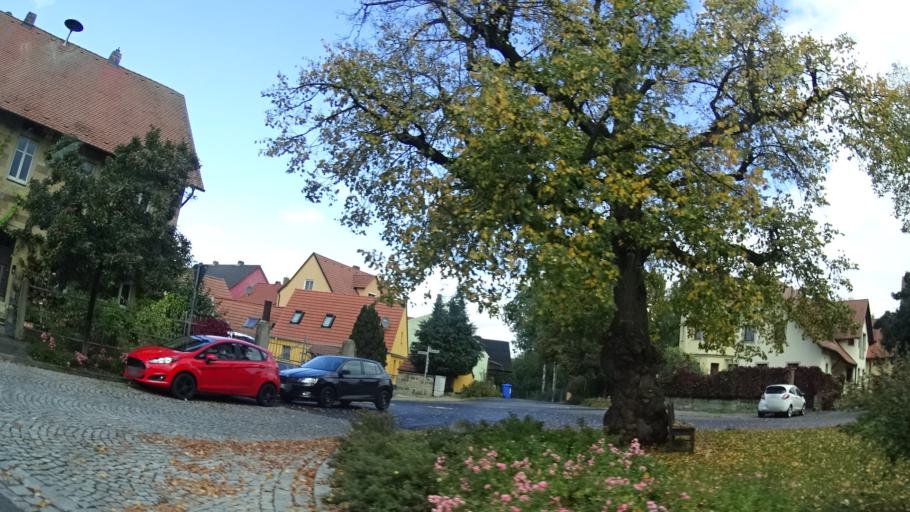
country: DE
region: Bavaria
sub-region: Regierungsbezirk Unterfranken
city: Frankenwinheim
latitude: 49.8639
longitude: 10.2942
